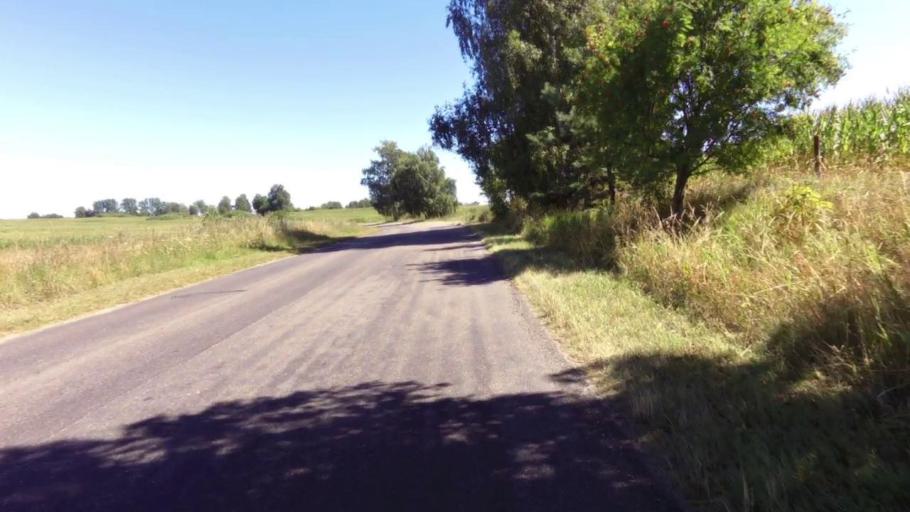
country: PL
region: West Pomeranian Voivodeship
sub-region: Powiat szczecinecki
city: Lubowo
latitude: 53.5851
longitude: 16.4126
